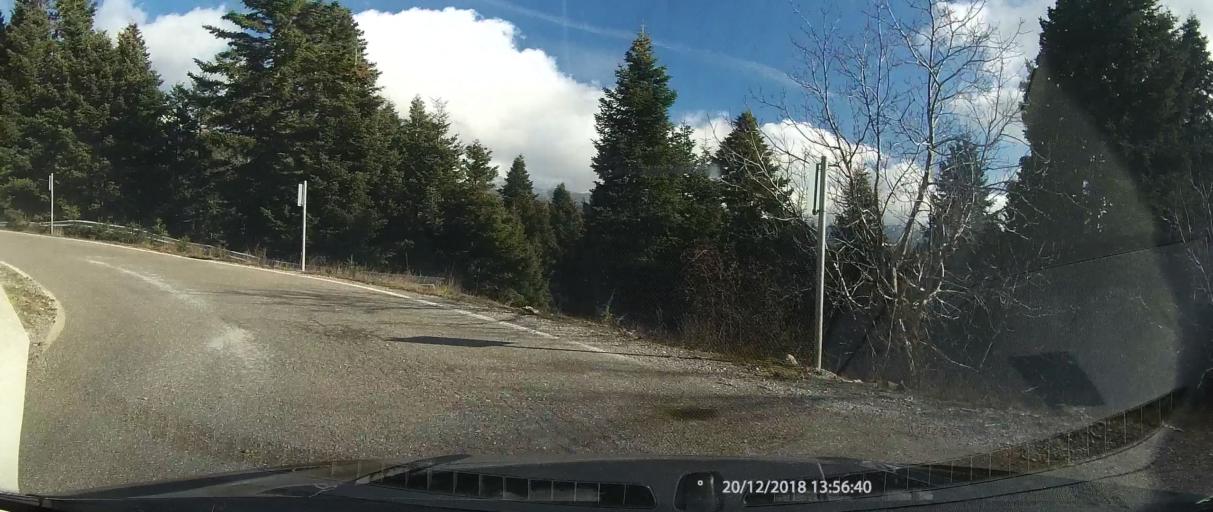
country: GR
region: West Greece
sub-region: Nomos Aitolias kai Akarnanias
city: Thermo
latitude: 38.7052
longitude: 21.6191
